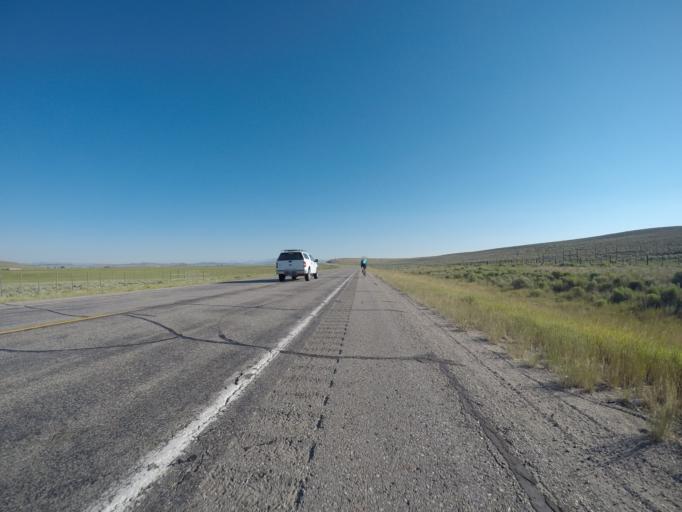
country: US
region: Wyoming
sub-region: Sublette County
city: Pinedale
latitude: 42.9319
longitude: -110.0812
